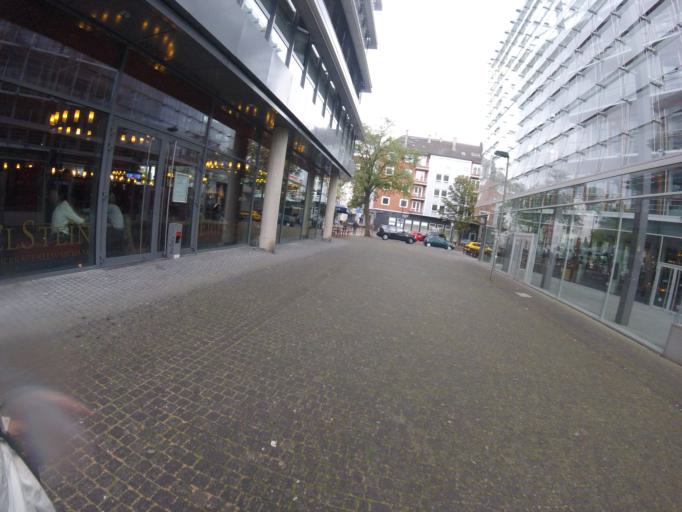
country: DE
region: North Rhine-Westphalia
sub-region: Regierungsbezirk Dusseldorf
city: Dusseldorf
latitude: 51.2145
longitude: 6.7548
